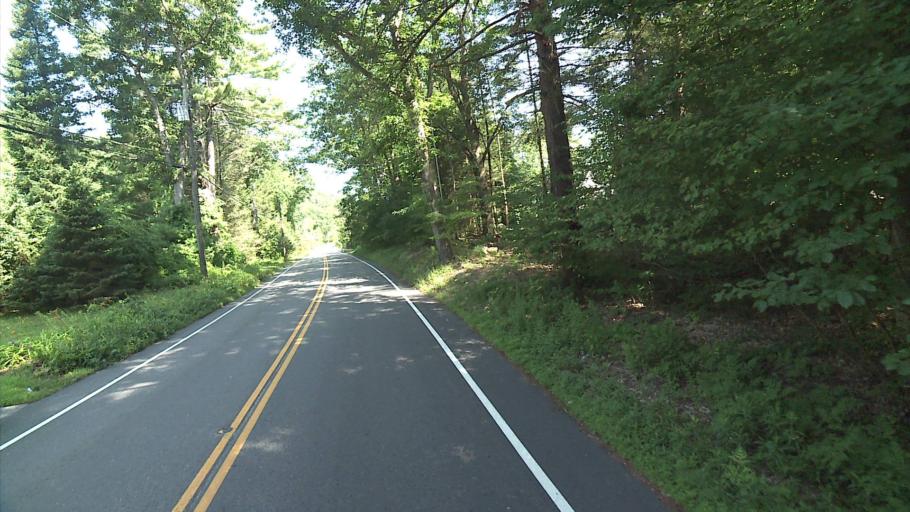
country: US
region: Connecticut
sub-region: Litchfield County
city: West Torrington
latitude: 41.8341
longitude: -73.1514
